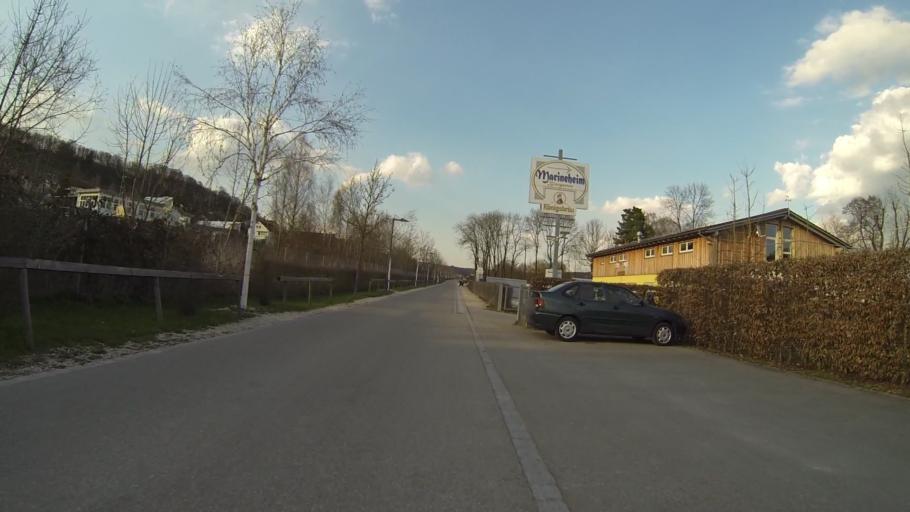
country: DE
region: Baden-Wuerttemberg
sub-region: Regierungsbezirk Stuttgart
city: Heidenheim an der Brenz
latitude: 48.6903
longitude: 10.1566
